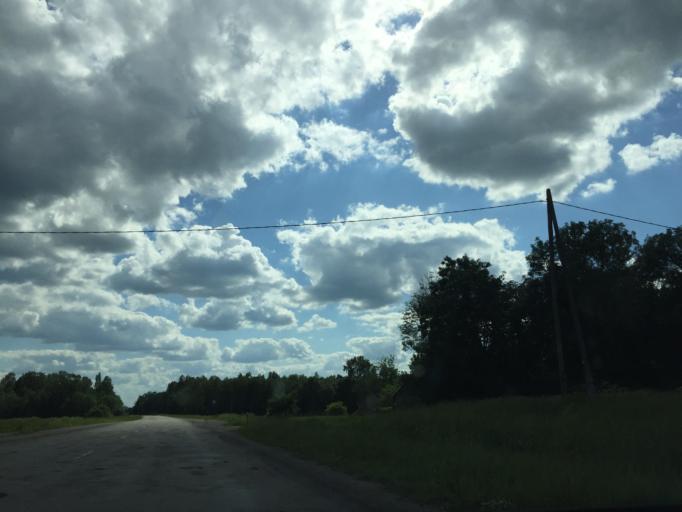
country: LV
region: Tukuma Rajons
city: Tukums
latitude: 56.8673
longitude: 23.0616
